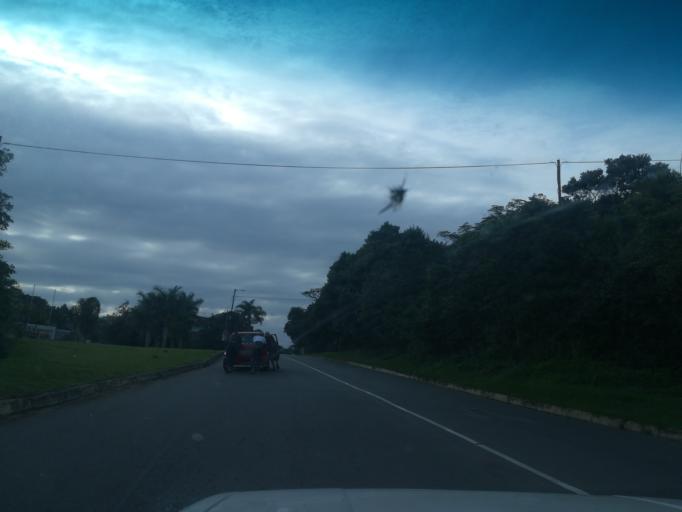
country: ZA
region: KwaZulu-Natal
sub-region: Ugu District Municipality
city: Scottburgh
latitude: -30.2852
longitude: 30.7479
